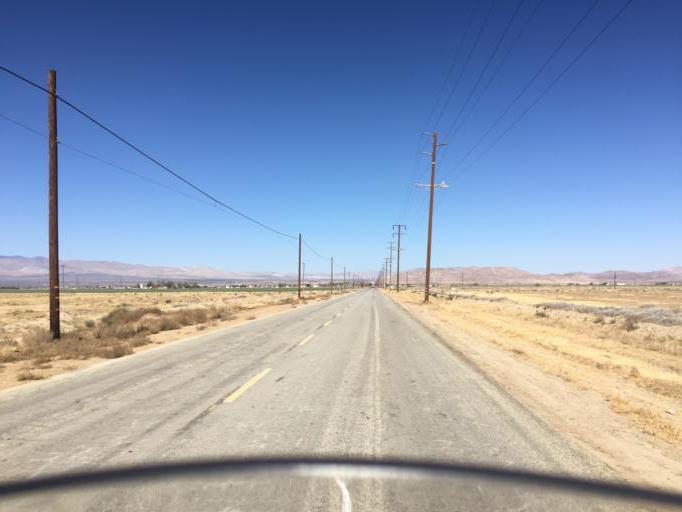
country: US
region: California
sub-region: Kern County
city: Rosamond
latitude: 34.8107
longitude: -118.2904
